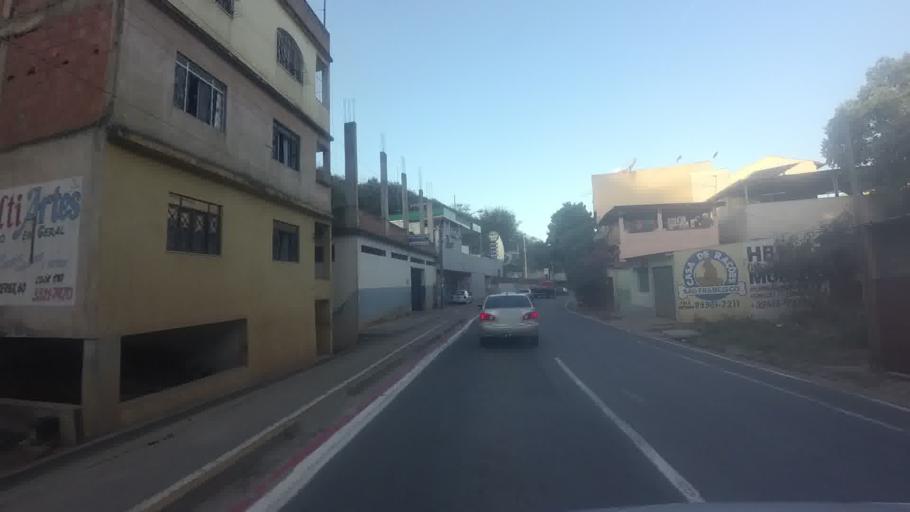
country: BR
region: Espirito Santo
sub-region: Cachoeiro De Itapemirim
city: Cachoeiro de Itapemirim
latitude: -20.8477
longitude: -41.1389
